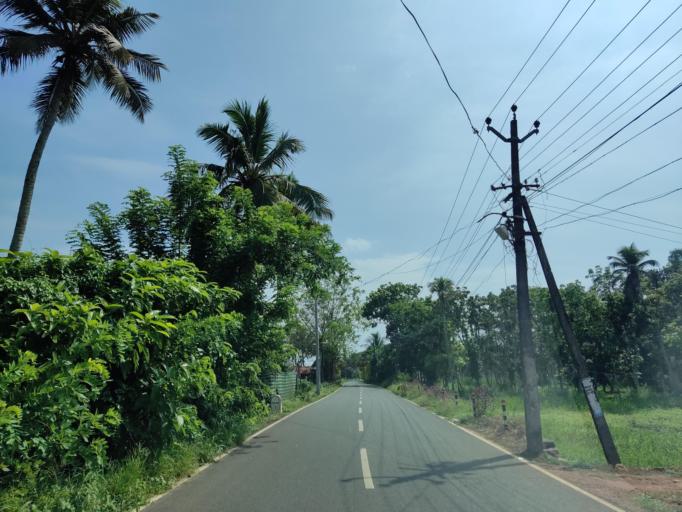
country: IN
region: Kerala
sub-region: Alappuzha
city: Mavelikara
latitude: 9.3262
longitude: 76.4702
